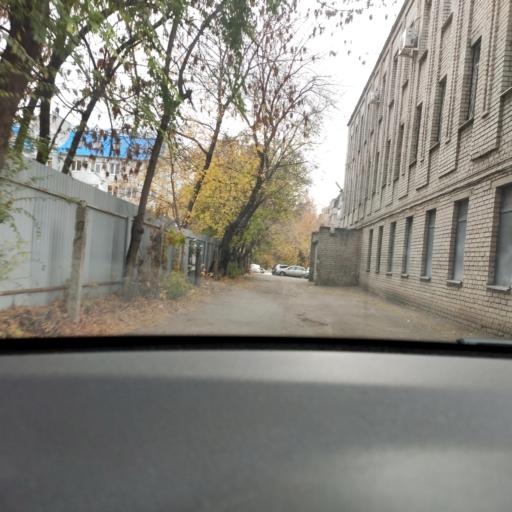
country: RU
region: Samara
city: Samara
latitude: 53.1980
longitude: 50.1648
